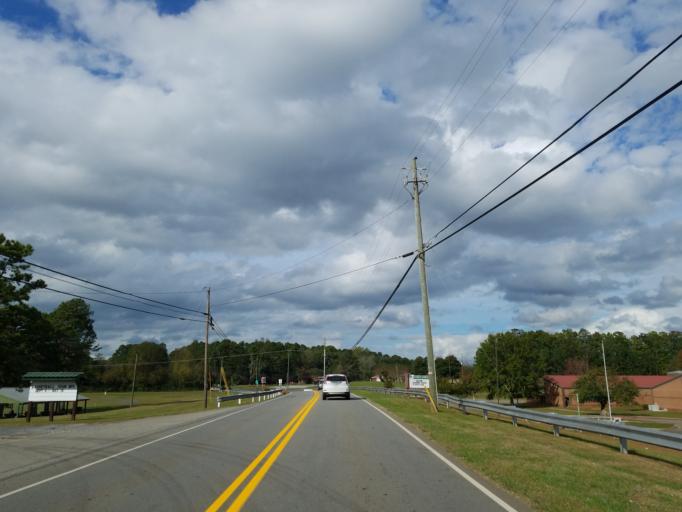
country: US
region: Georgia
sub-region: Pickens County
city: Jasper
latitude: 34.4435
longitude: -84.4211
